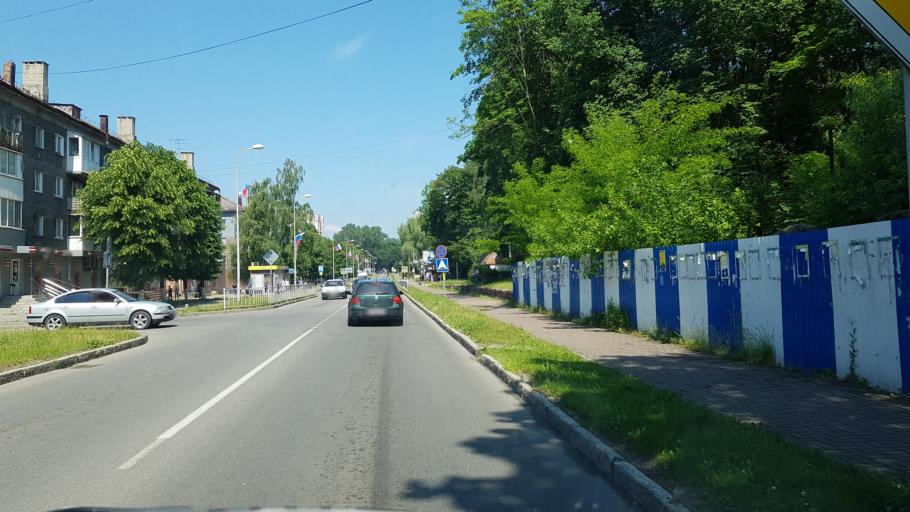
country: RU
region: Kaliningrad
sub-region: Gorod Kaliningrad
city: Baltiysk
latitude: 54.6585
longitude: 19.9138
